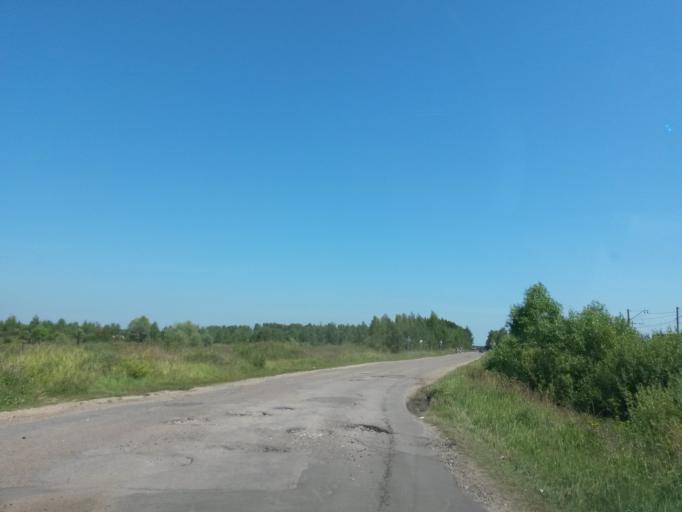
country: RU
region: Moskovskaya
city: Stolbovaya
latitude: 55.2585
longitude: 37.4821
